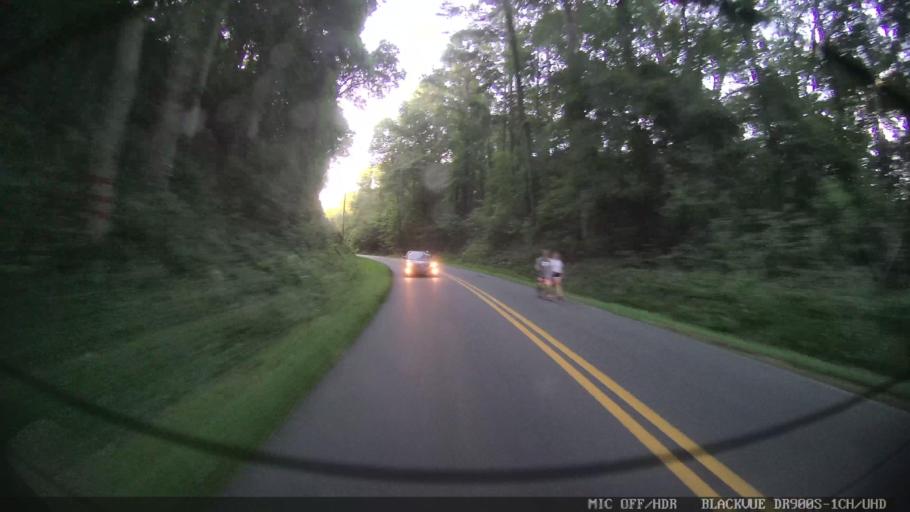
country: US
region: Georgia
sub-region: Bartow County
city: Emerson
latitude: 34.0961
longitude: -84.7231
